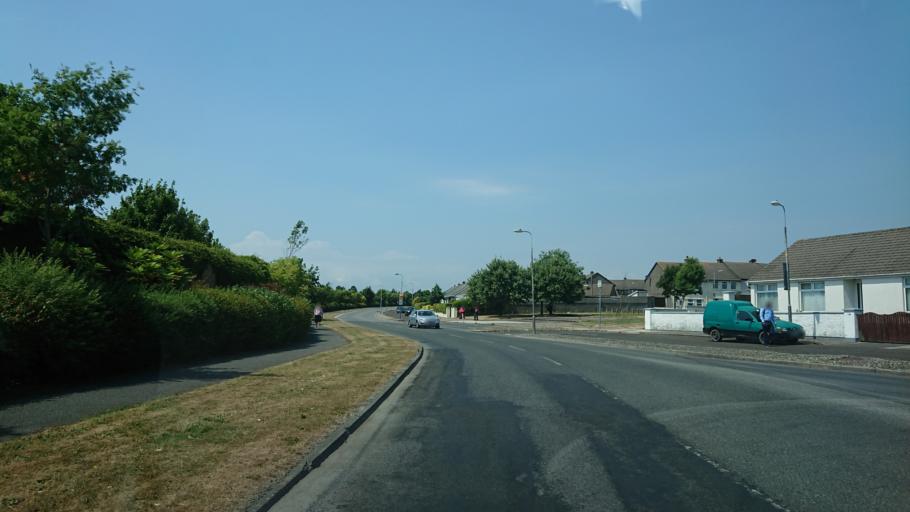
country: IE
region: Munster
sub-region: Waterford
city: Waterford
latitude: 52.2471
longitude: -7.1364
